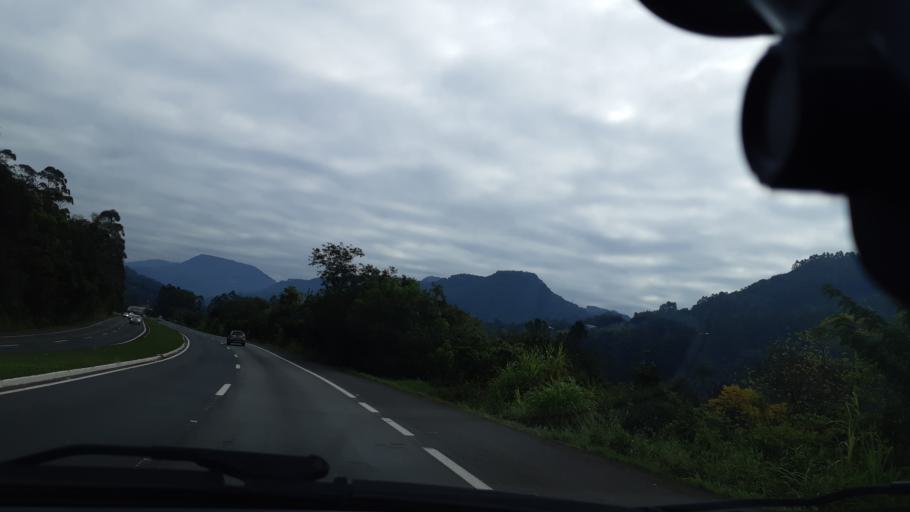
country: BR
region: Rio Grande do Sul
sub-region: Sao Sebastiao Do Cai
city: Sao Sebastiao do Cai
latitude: -29.4068
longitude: -51.3527
